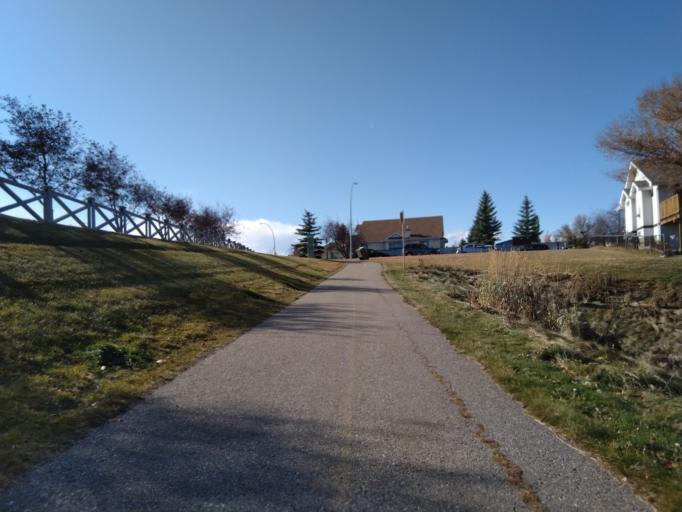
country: CA
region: Alberta
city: Calgary
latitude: 51.1471
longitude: -114.1143
